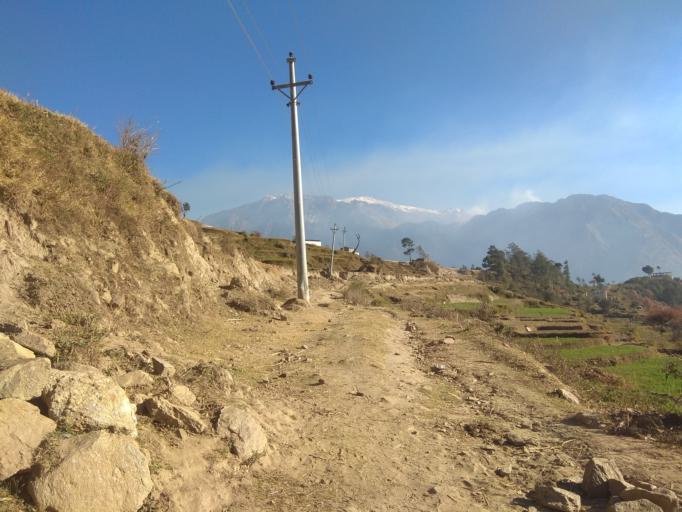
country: NP
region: Far Western
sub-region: Seti Zone
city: Achham
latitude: 29.2501
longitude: 81.6425
